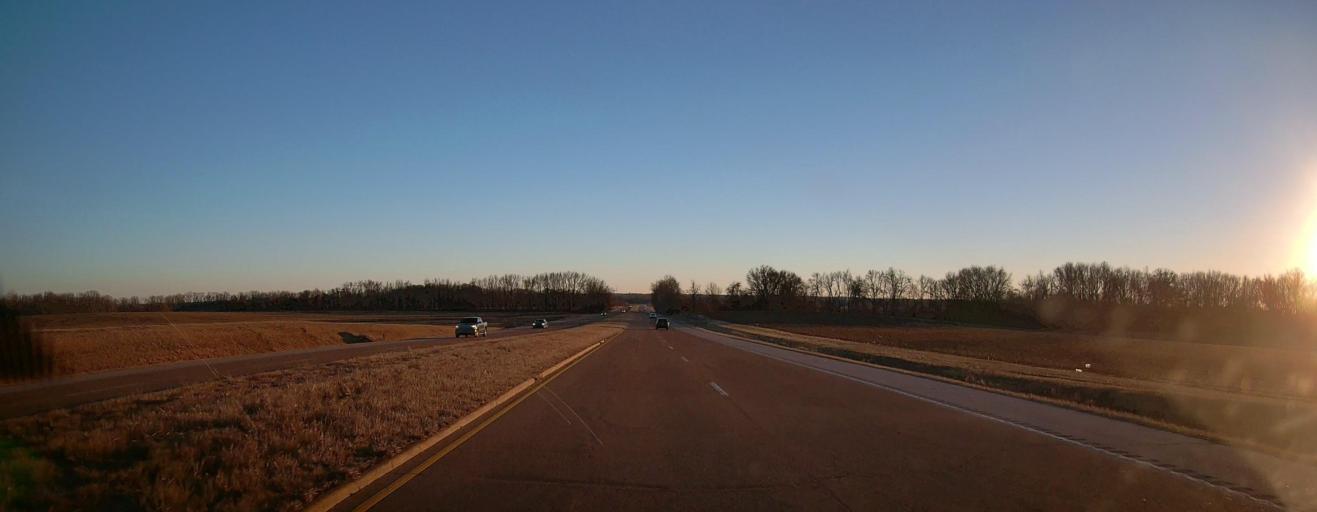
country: US
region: Tennessee
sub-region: Shelby County
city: Millington
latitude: 35.3039
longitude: -89.8820
